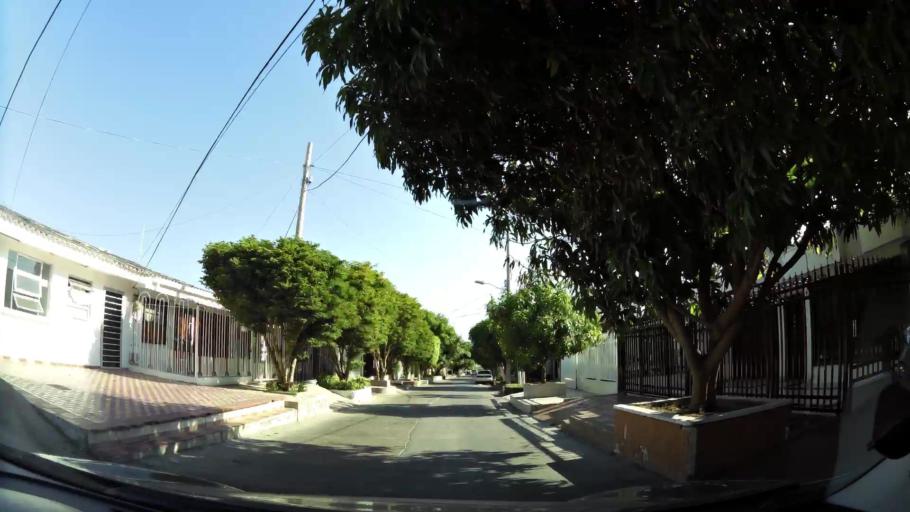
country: CO
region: Atlantico
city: Barranquilla
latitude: 11.0185
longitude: -74.8029
